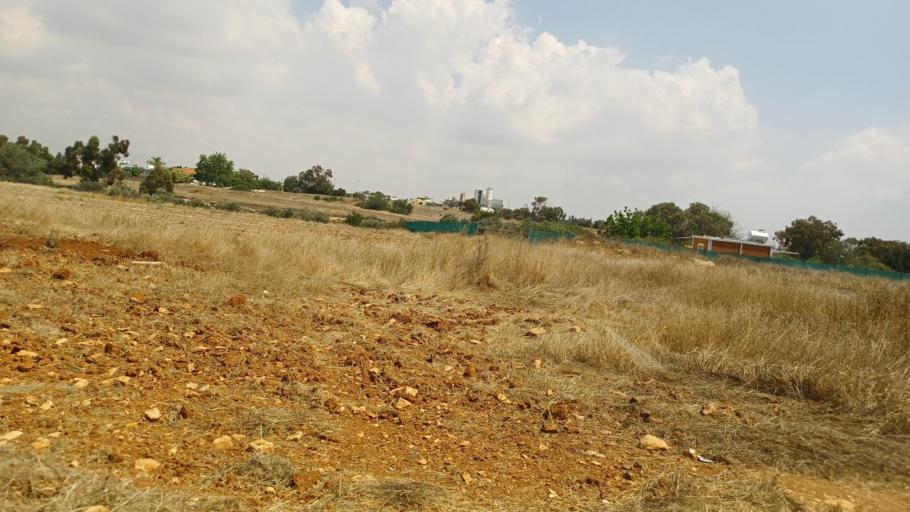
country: CY
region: Ammochostos
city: Liopetri
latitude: 34.9850
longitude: 33.8616
